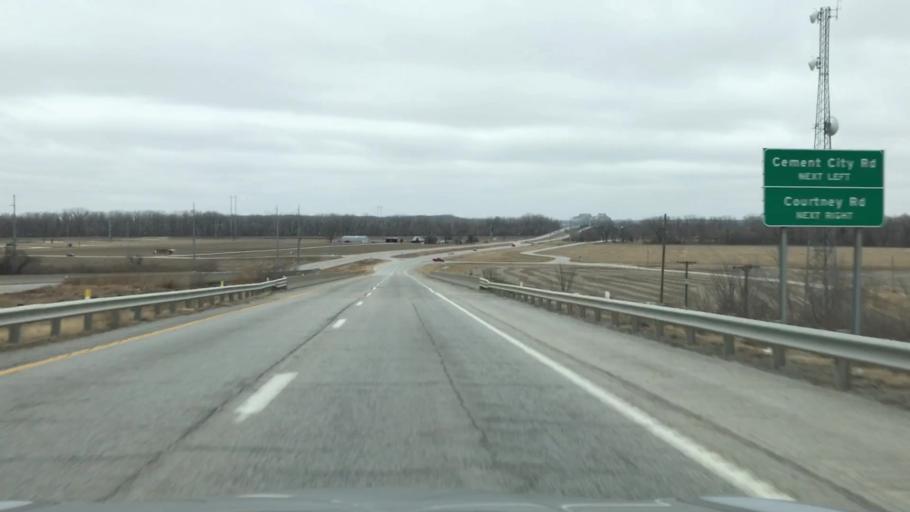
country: US
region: Missouri
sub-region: Jackson County
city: Independence
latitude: 39.1549
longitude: -94.3941
